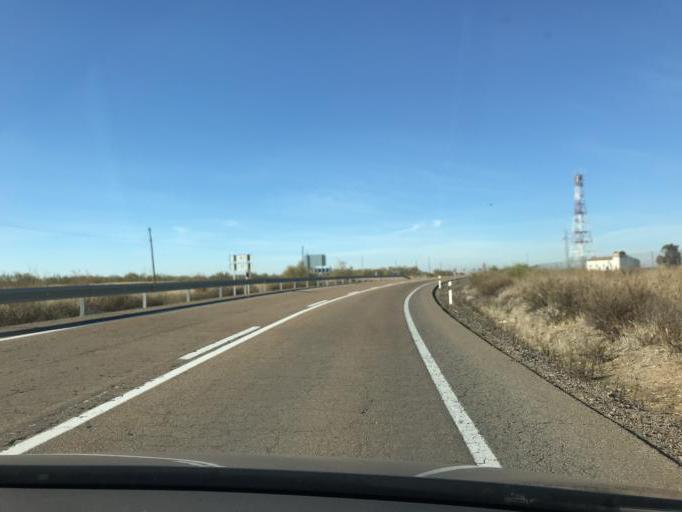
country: ES
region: Extremadura
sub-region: Provincia de Badajoz
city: Azuaga
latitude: 38.2589
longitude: -5.7163
